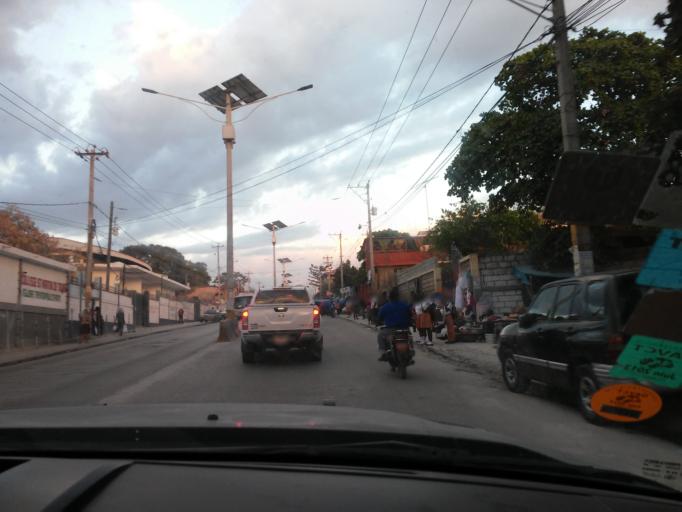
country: HT
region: Ouest
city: Port-au-Prince
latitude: 18.5563
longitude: -72.3233
